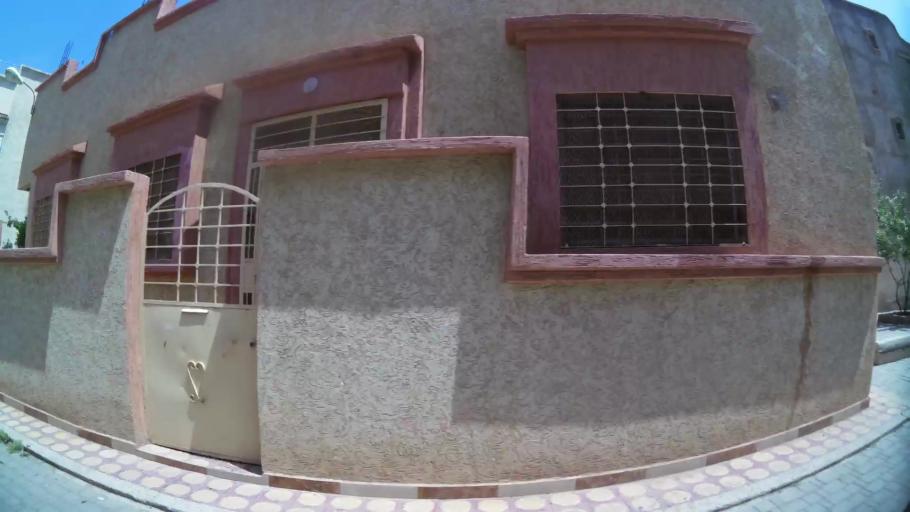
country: MA
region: Oriental
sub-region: Oujda-Angad
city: Oujda
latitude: 34.6895
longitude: -1.8890
